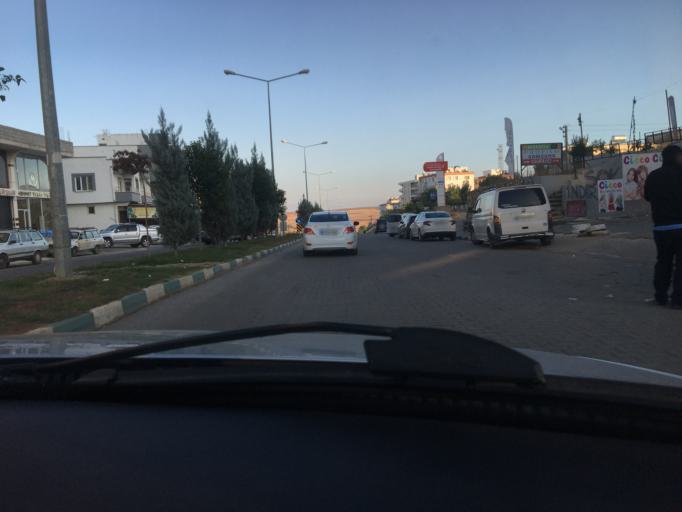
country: TR
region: Sanliurfa
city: Halfeti
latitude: 37.2308
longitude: 37.9463
